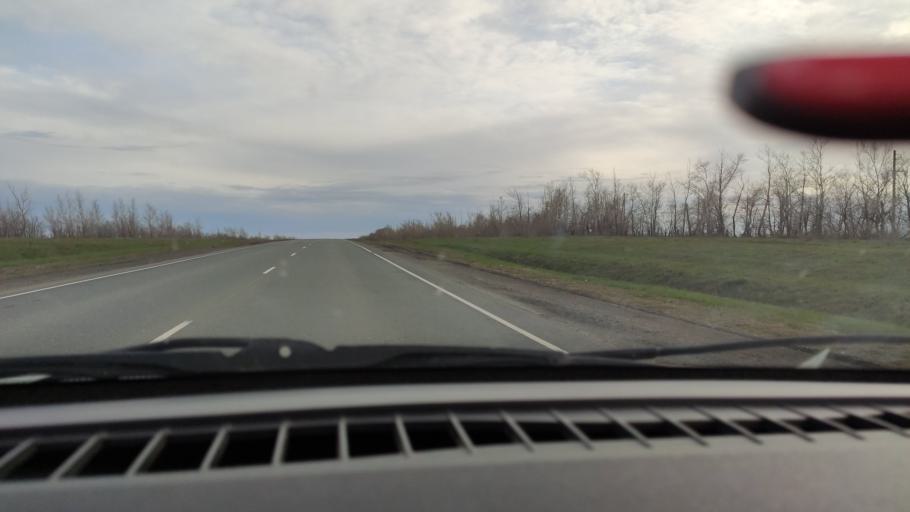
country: RU
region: Orenburg
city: Sakmara
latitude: 52.0708
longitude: 55.2624
